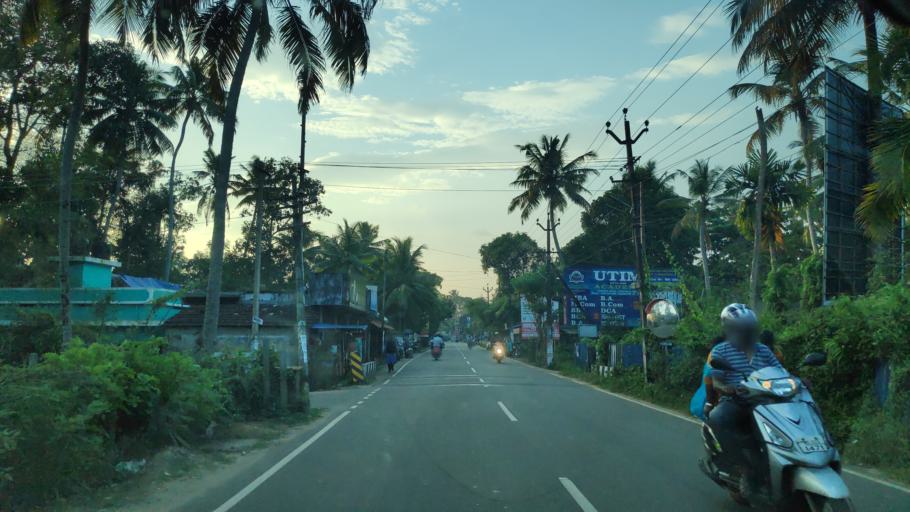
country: IN
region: Kerala
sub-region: Alappuzha
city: Shertallai
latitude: 9.6822
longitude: 76.3525
